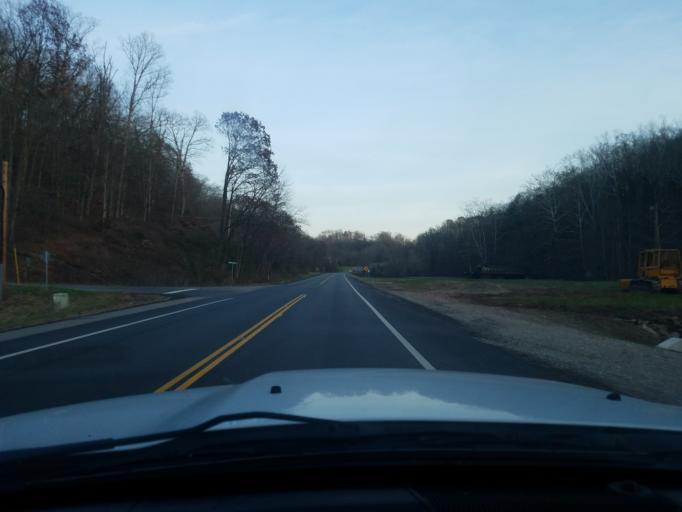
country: US
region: Ohio
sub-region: Washington County
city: Marietta
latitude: 39.4072
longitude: -81.4881
